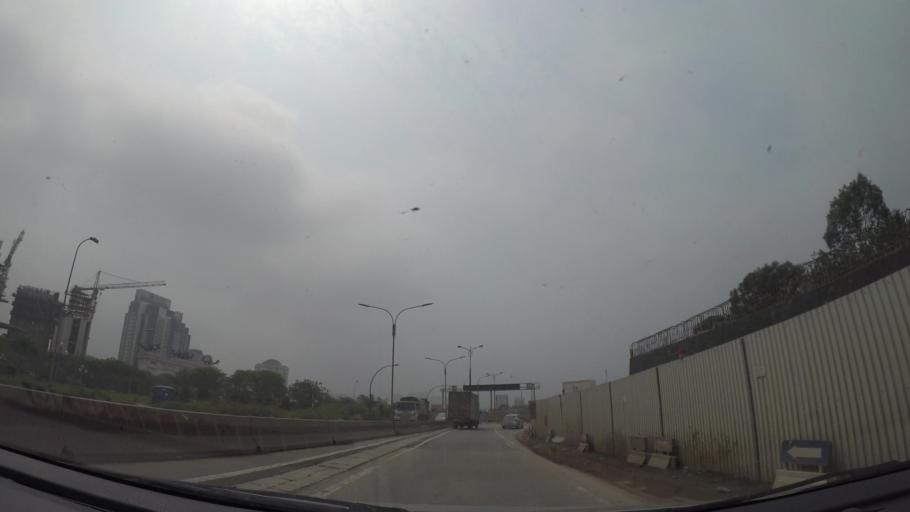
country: VN
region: Ha Noi
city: Tay Ho
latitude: 21.0823
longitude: 105.7883
